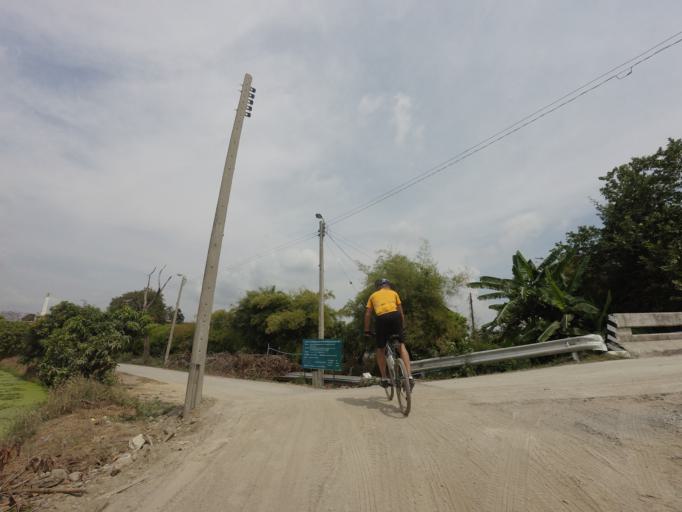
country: TH
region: Bangkok
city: Lat Krabang
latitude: 13.6669
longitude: 100.7655
